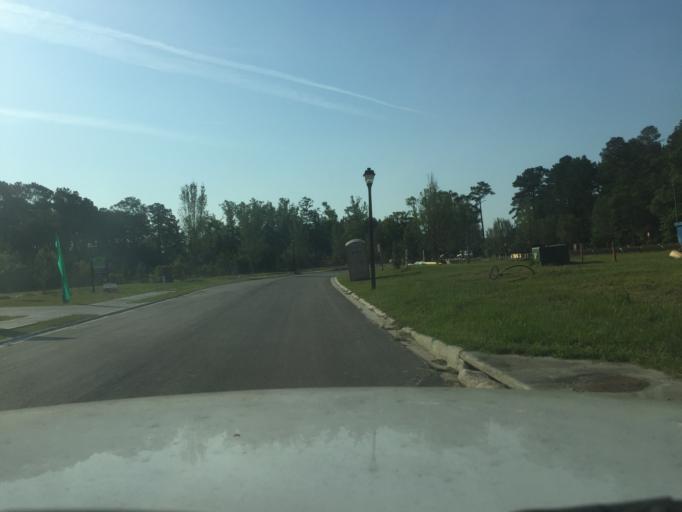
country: US
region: Georgia
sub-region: Chatham County
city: Georgetown
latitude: 32.0373
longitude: -81.2211
